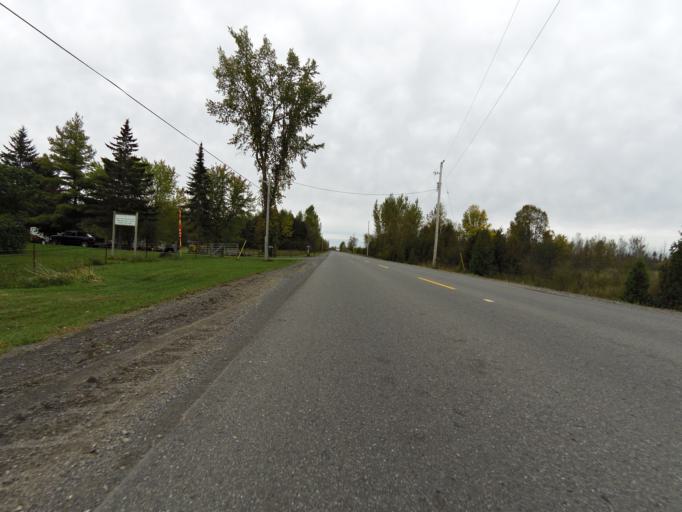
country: CA
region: Ontario
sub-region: Lanark County
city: Smiths Falls
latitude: 44.8302
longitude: -75.8159
